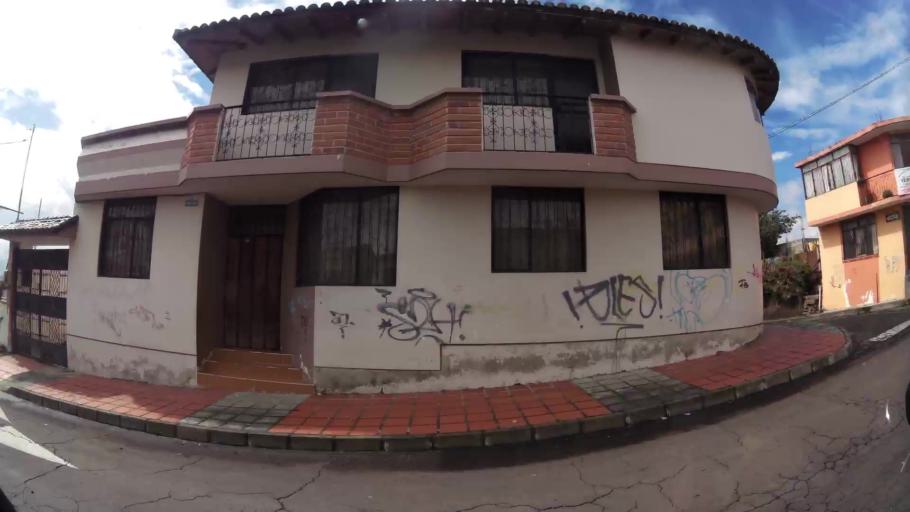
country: EC
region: Pichincha
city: Sangolqui
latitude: -0.3080
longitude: -78.4162
